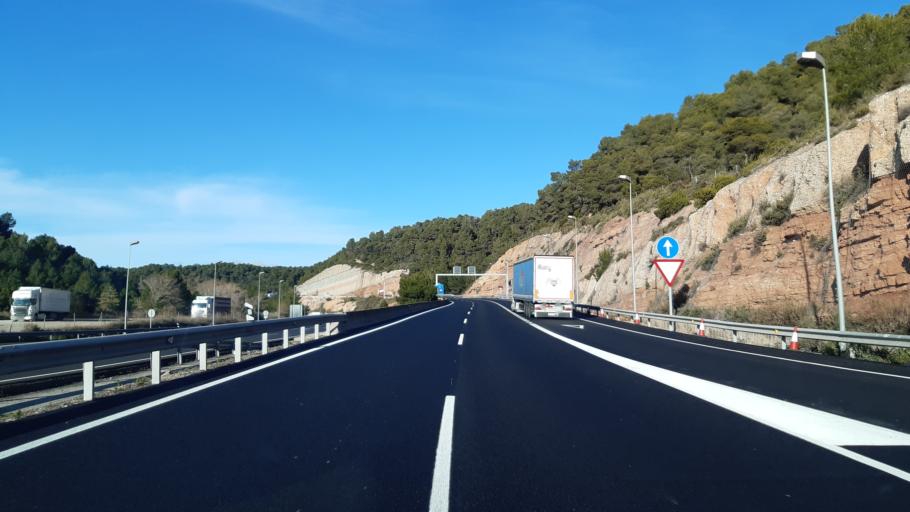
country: ES
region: Catalonia
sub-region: Provincia de Barcelona
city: Castelloli
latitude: 41.5941
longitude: 1.7495
